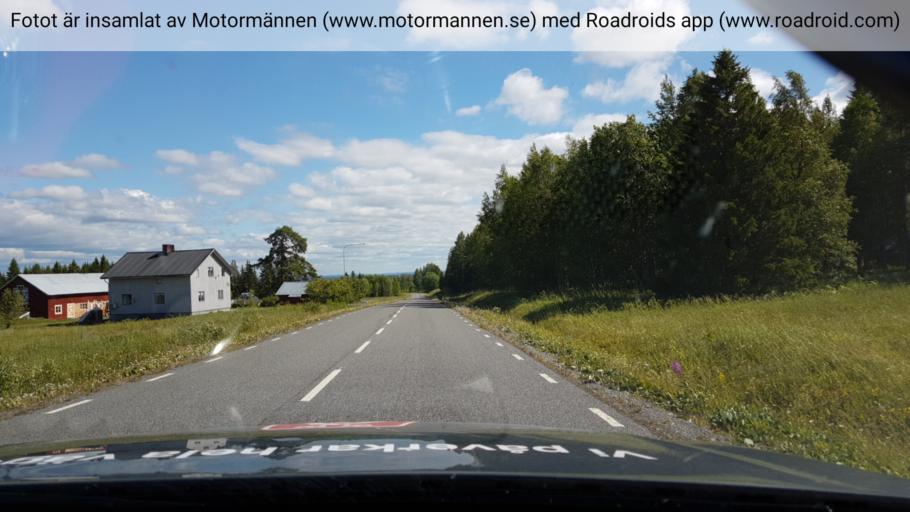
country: SE
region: Jaemtland
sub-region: OEstersunds Kommun
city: Lit
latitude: 63.3643
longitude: 15.2000
